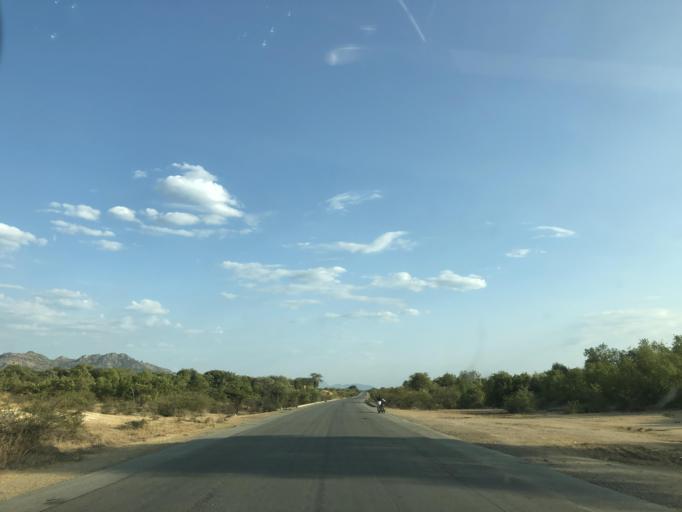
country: AO
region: Huila
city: Caluquembe
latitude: -13.5024
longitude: 13.9162
